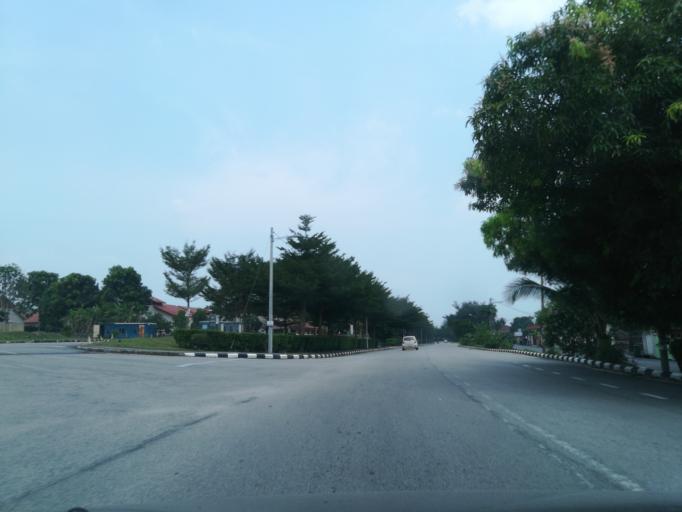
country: MY
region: Kedah
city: Kulim
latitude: 5.4022
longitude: 100.5666
